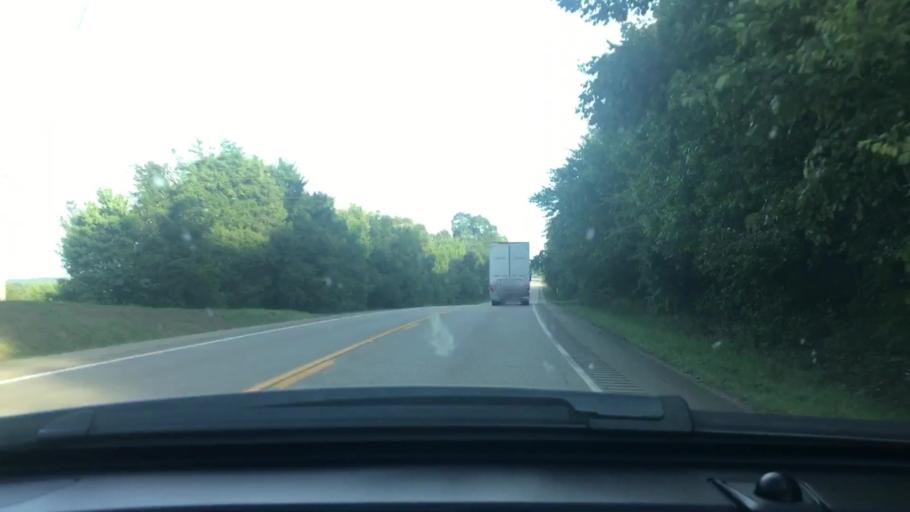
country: US
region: Arkansas
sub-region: Randolph County
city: Pocahontas
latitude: 36.2124
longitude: -91.2050
